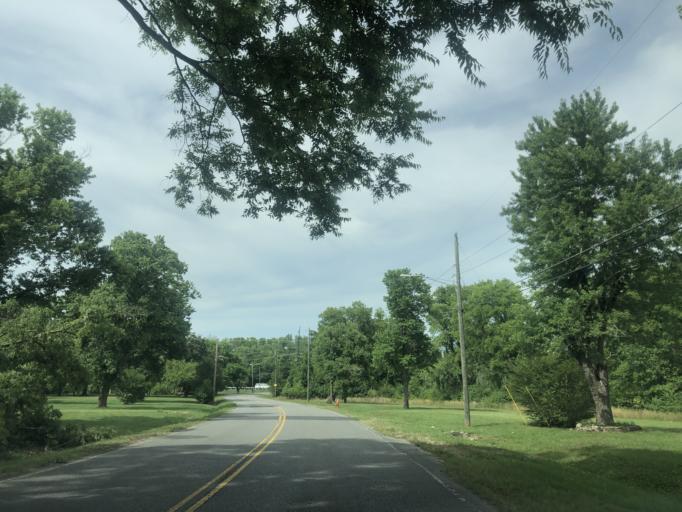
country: US
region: Tennessee
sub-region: Davidson County
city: Nashville
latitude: 36.2165
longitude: -86.8217
